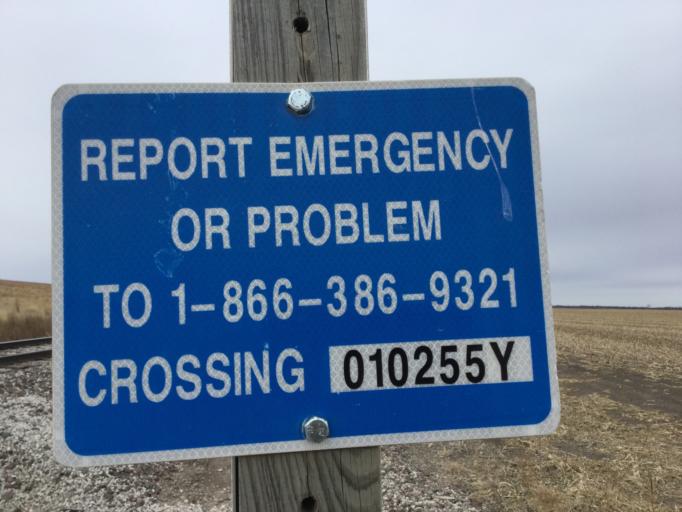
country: US
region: Kansas
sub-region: Rush County
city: La Crosse
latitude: 38.4679
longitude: -99.0700
